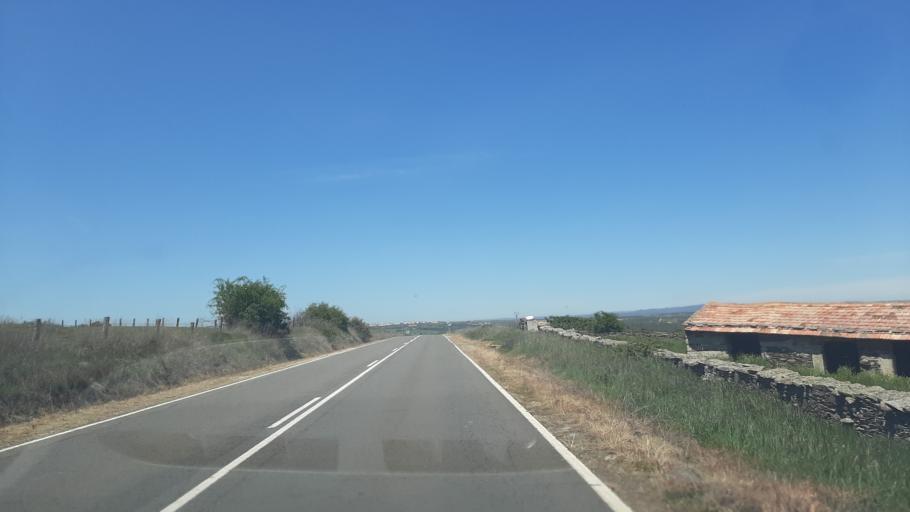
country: ES
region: Castille and Leon
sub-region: Provincia de Salamanca
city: Salvatierra de Tormes
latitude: 40.5433
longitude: -5.5897
